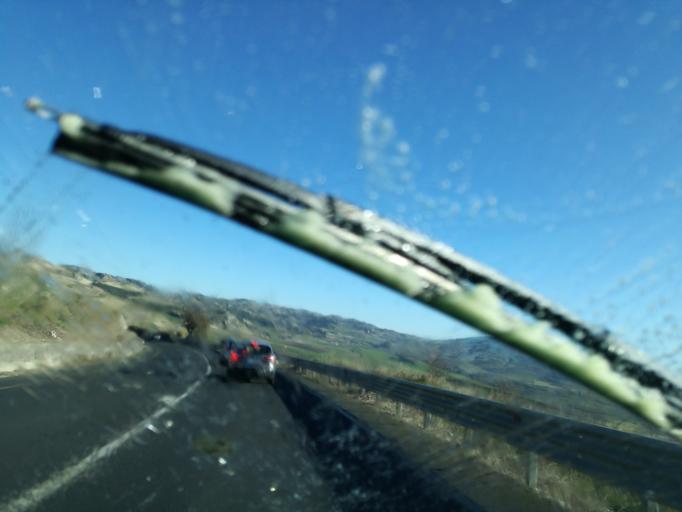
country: IT
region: Sicily
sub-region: Catania
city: San Michele di Ganzaria
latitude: 37.2307
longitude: 14.4466
